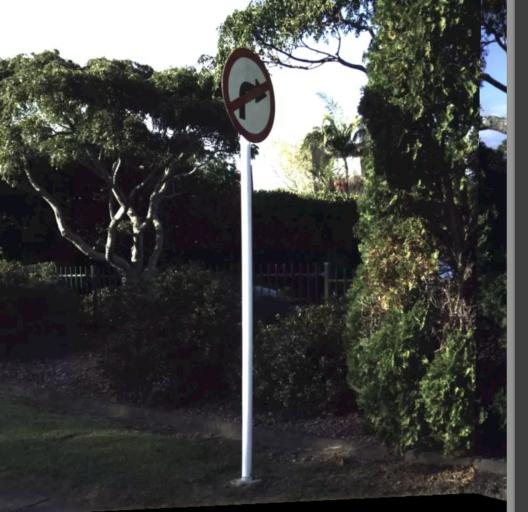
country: NZ
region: Auckland
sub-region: Auckland
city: Tamaki
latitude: -36.8600
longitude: 174.8310
